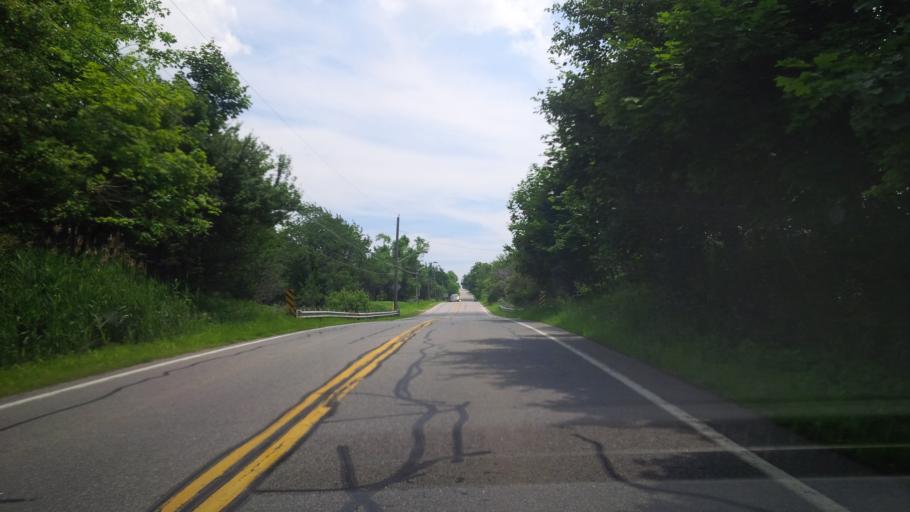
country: CA
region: Ontario
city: Burlington
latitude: 43.4268
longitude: -79.8973
